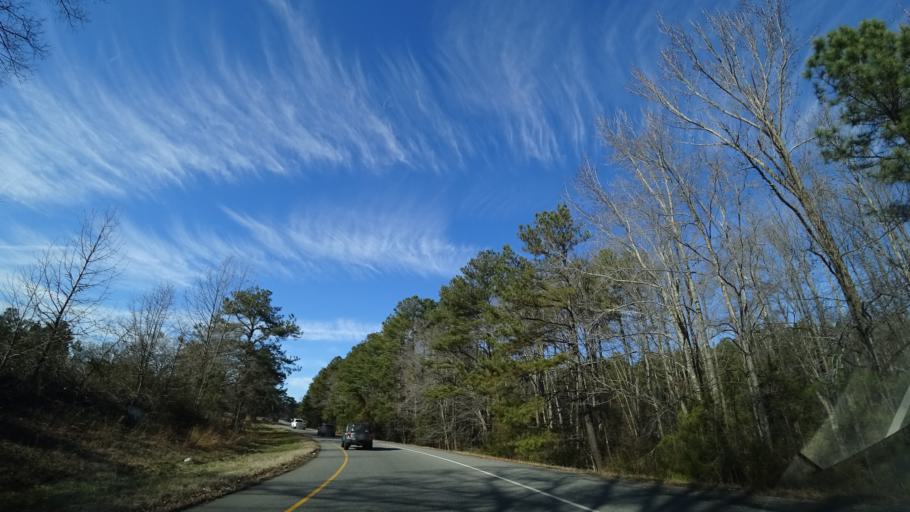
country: US
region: Virginia
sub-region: Hanover County
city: Ashland
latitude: 37.7614
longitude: -77.4575
